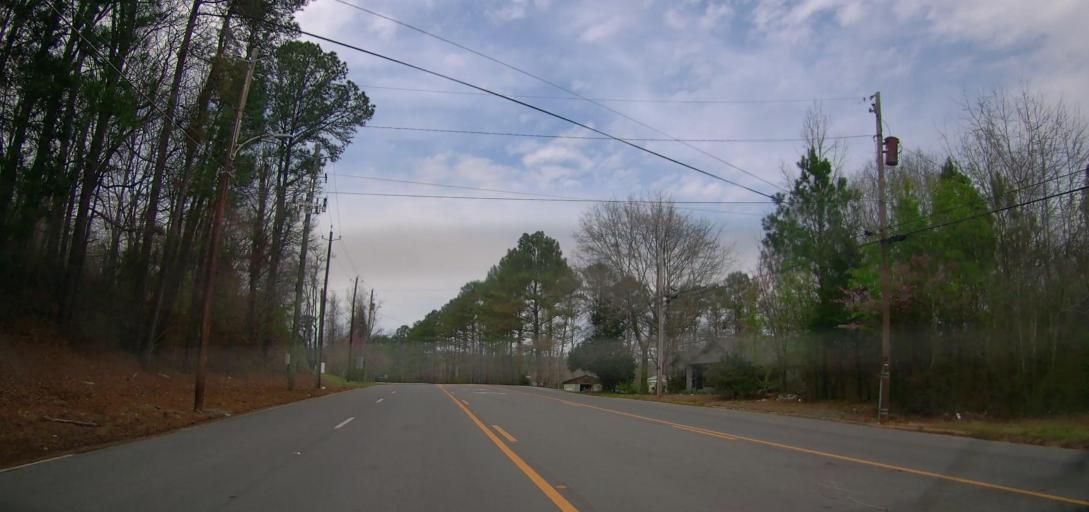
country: US
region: Alabama
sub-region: Marion County
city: Guin
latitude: 33.9810
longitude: -87.9177
